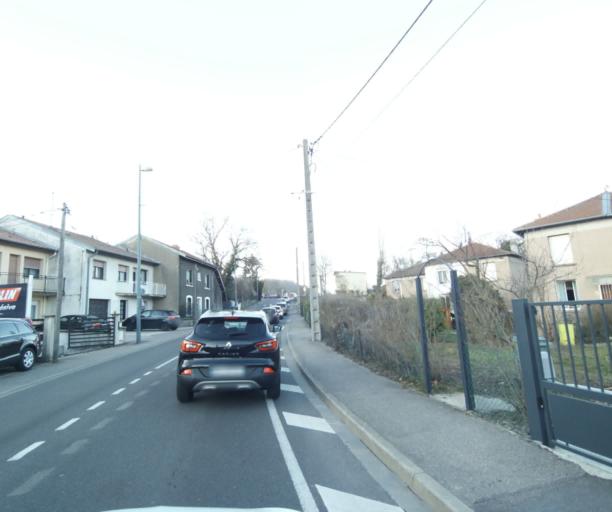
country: FR
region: Lorraine
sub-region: Departement de Meurthe-et-Moselle
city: Maxeville
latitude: 48.7112
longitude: 6.1694
